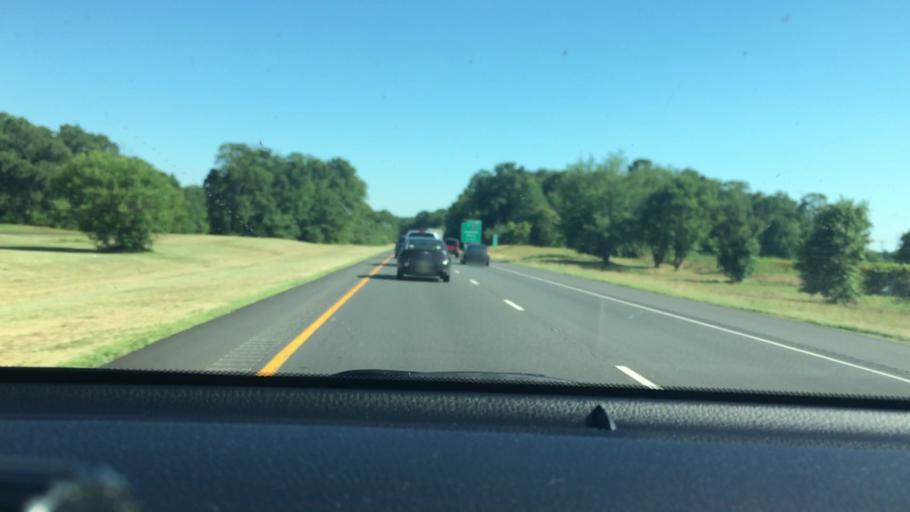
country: US
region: New Jersey
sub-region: Gloucester County
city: Richwood
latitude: 39.7080
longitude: -75.1537
